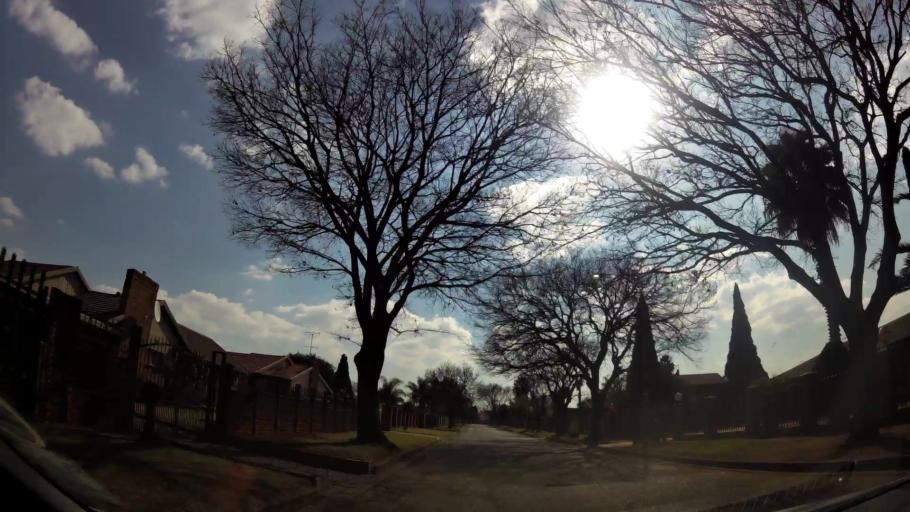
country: ZA
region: Gauteng
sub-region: Ekurhuleni Metropolitan Municipality
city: Germiston
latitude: -26.1939
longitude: 28.2080
